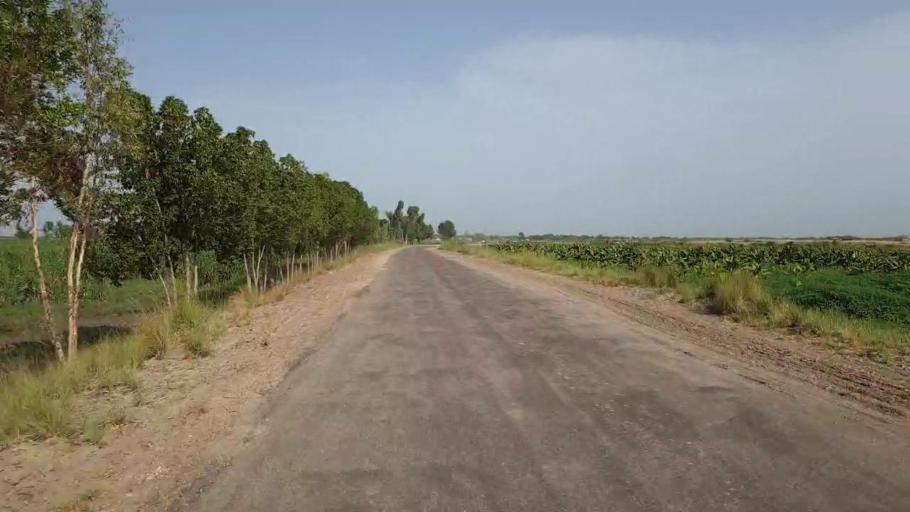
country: PK
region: Sindh
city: Sakrand
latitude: 26.2791
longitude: 68.2696
